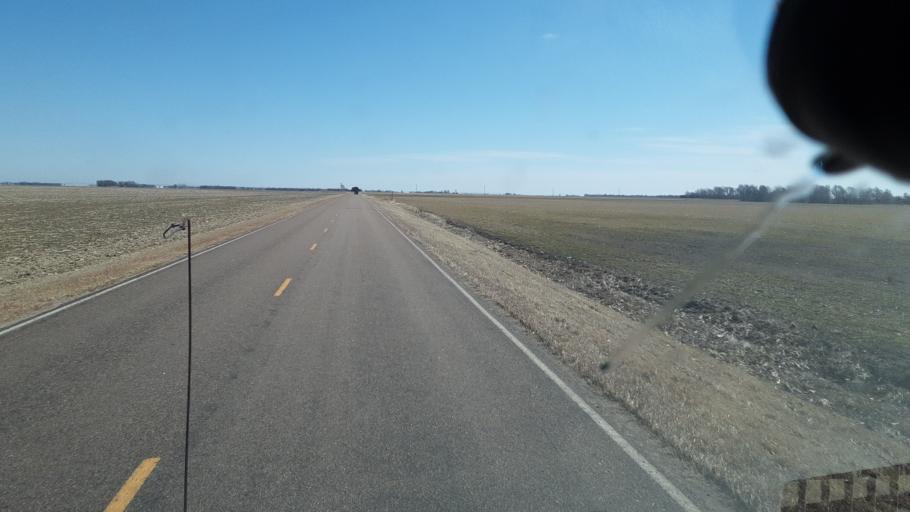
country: US
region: Kansas
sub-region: Rice County
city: Sterling
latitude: 38.2461
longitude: -98.2788
